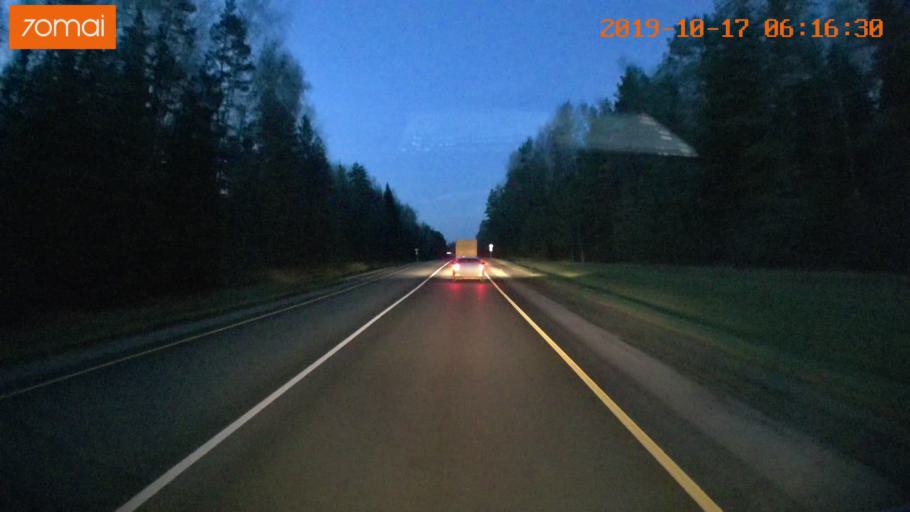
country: RU
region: Ivanovo
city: Lezhnevo
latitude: 56.8615
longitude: 40.9314
